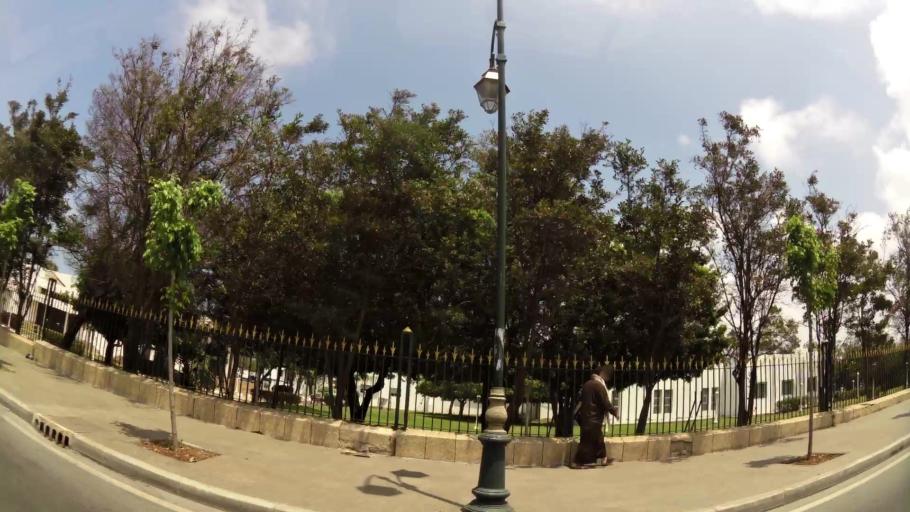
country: MA
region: Rabat-Sale-Zemmour-Zaer
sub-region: Skhirate-Temara
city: Temara
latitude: 33.9738
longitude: -6.8822
